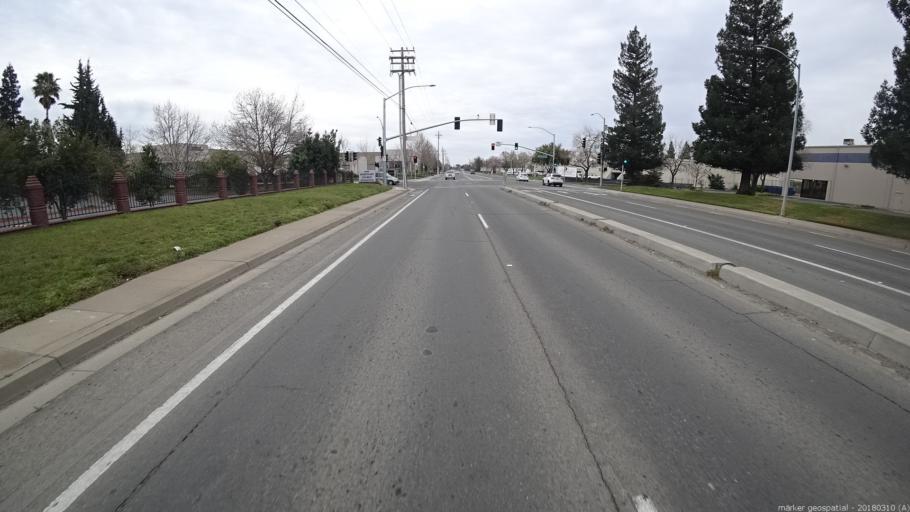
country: US
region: California
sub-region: Sacramento County
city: Florin
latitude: 38.5066
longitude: -121.3906
